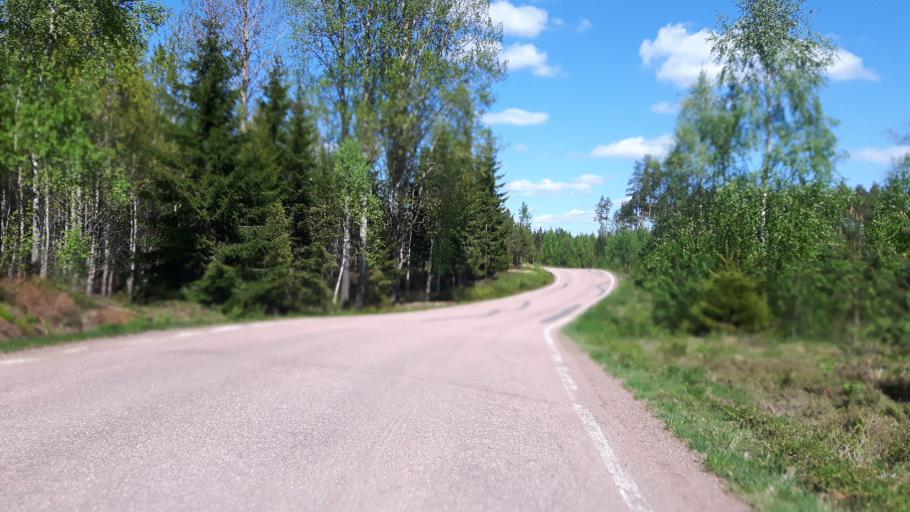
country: FI
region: Kymenlaakso
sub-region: Kotka-Hamina
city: Virolahti
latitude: 60.5367
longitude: 27.6171
